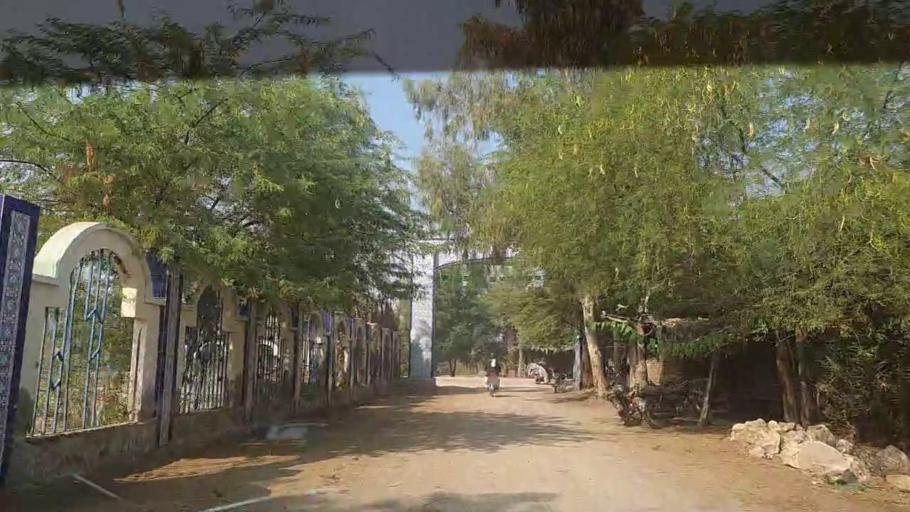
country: PK
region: Sindh
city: Khairpur
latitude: 27.4715
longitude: 68.7087
